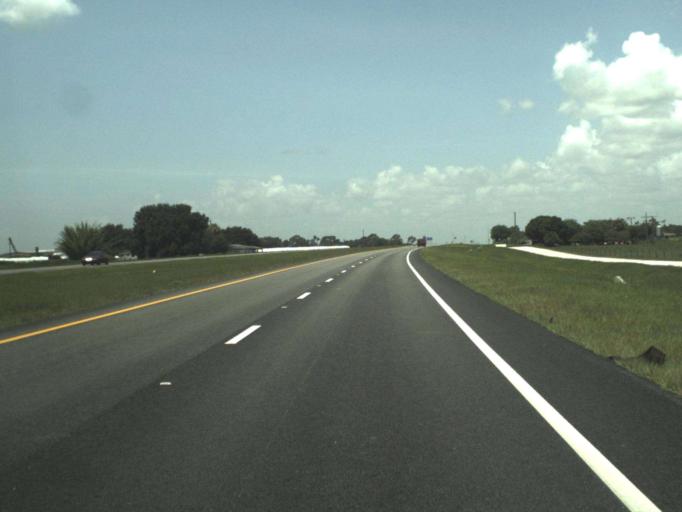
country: US
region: Florida
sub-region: Okeechobee County
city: Taylor Creek
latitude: 27.3062
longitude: -80.6708
